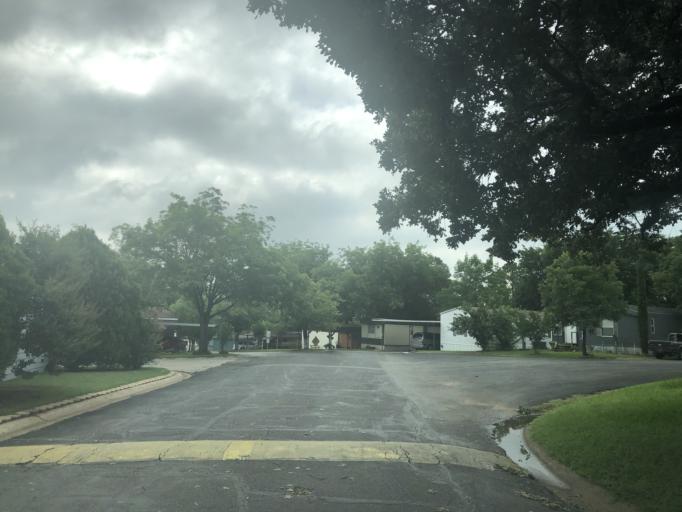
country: US
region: Texas
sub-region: Dallas County
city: Irving
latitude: 32.8086
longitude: -96.9969
